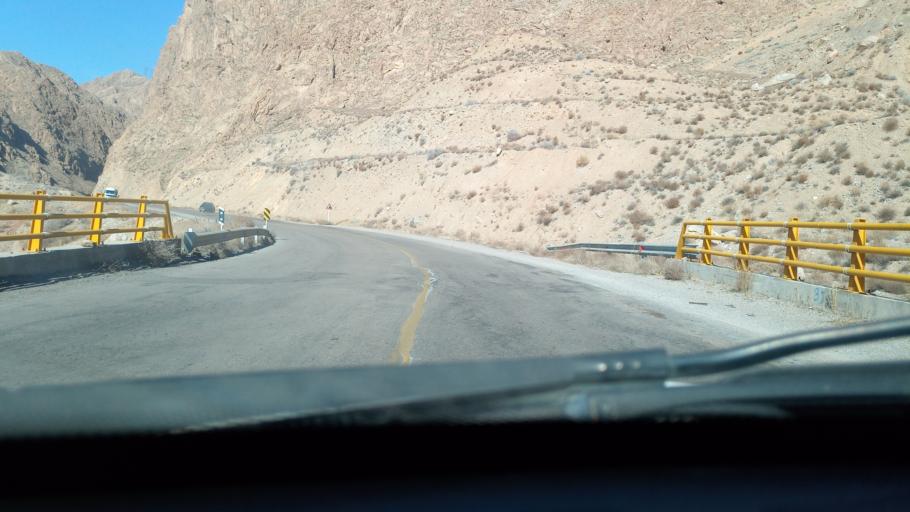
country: IR
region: Khorasan-e Shomali
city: Esfarayen
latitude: 37.1700
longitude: 57.4276
